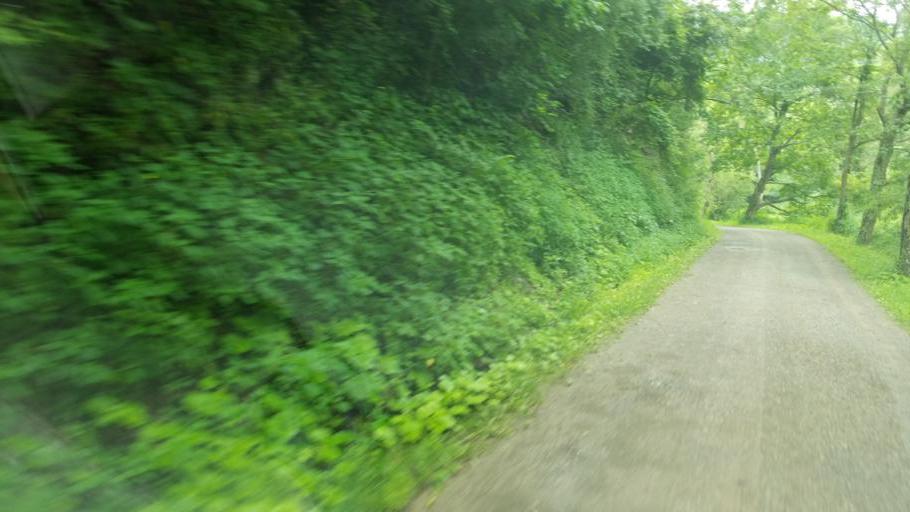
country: US
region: Ohio
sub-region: Columbiana County
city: Salineville
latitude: 40.5595
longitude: -80.8054
